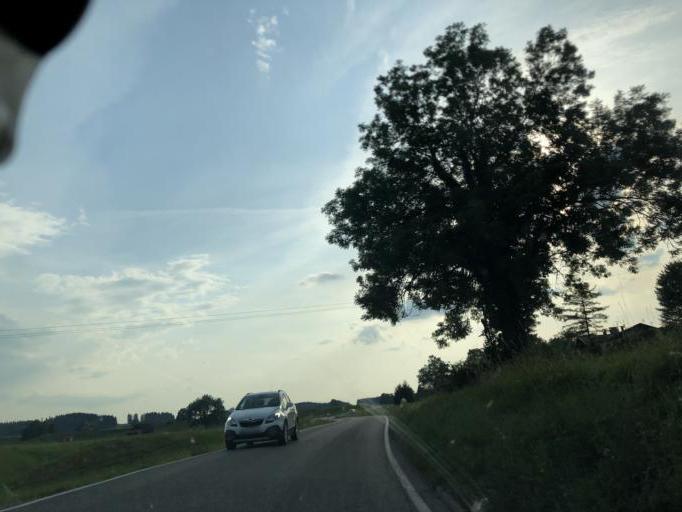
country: DE
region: Bavaria
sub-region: Swabia
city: Unterthingau
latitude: 47.7552
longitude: 10.5332
